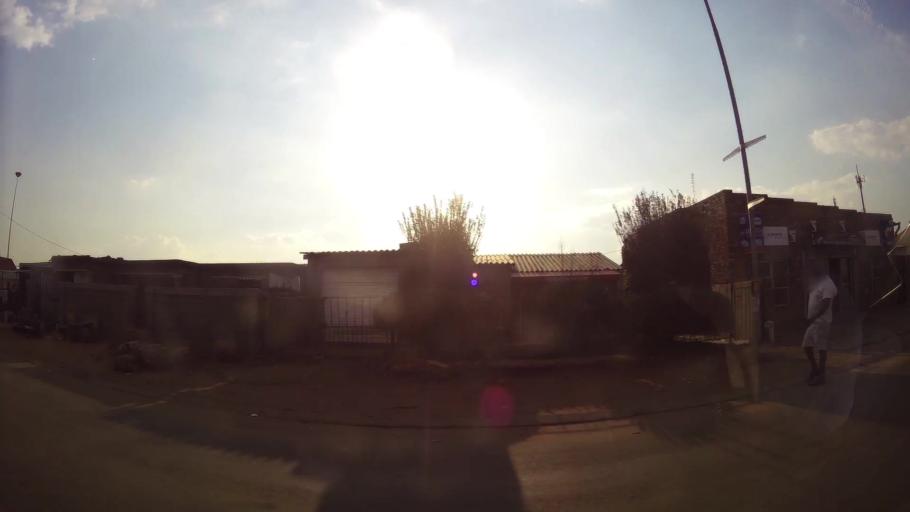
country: ZA
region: Gauteng
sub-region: Ekurhuleni Metropolitan Municipality
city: Germiston
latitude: -26.3519
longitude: 28.1987
